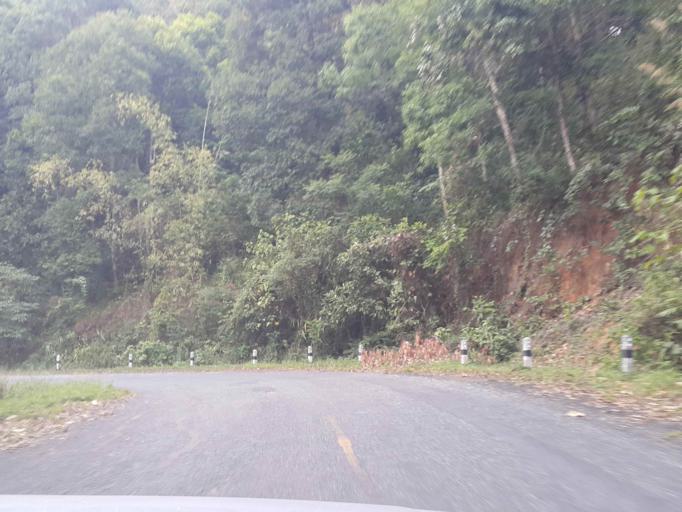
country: TH
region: Chiang Mai
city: Mae On
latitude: 18.9935
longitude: 99.3427
